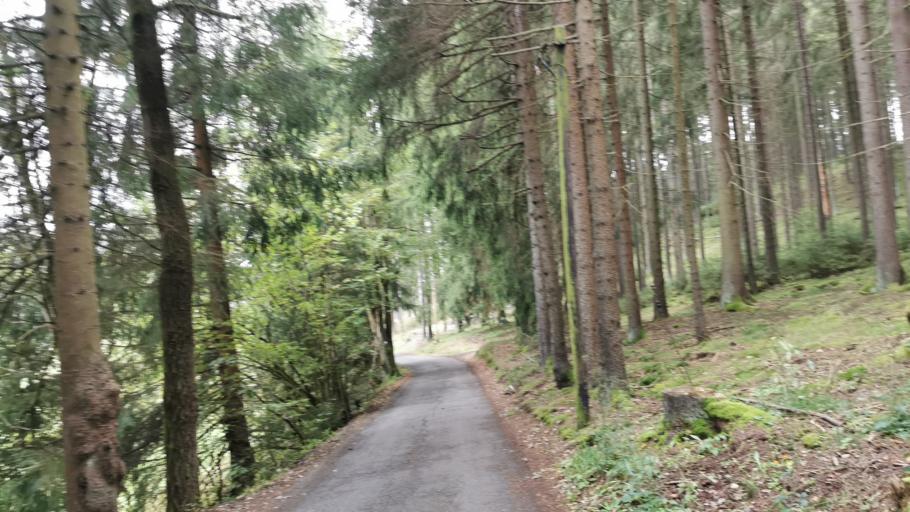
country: DE
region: Bavaria
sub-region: Upper Franconia
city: Teuschnitz
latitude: 50.4243
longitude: 11.3807
